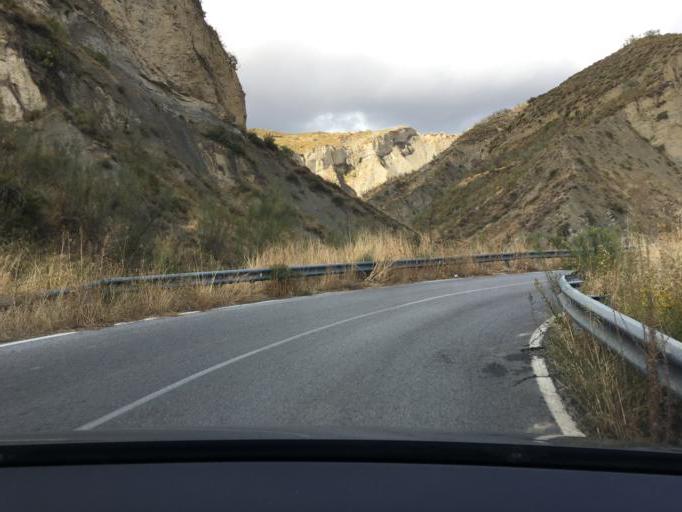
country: ES
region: Andalusia
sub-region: Provincia de Granada
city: Quentar
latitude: 37.1969
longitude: -3.4729
